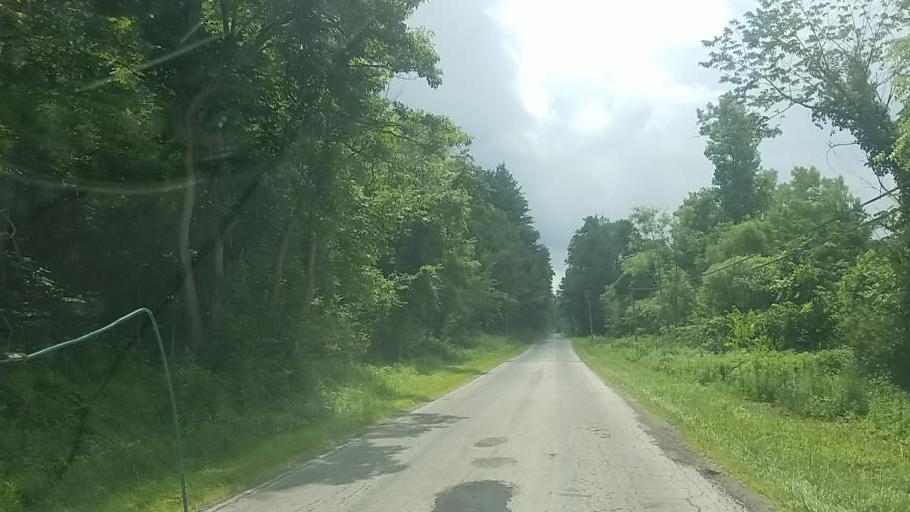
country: US
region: Ohio
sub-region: Muskingum County
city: Frazeysburg
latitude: 40.2057
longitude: -82.2596
